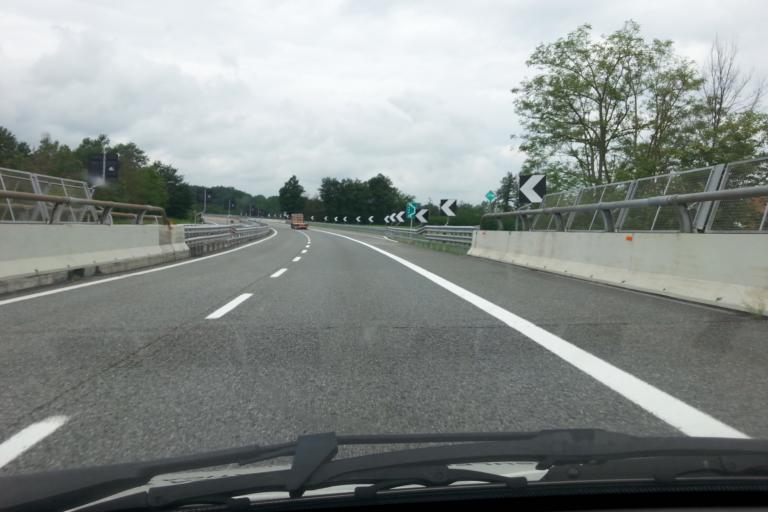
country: IT
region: Piedmont
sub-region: Provincia di Cuneo
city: Lesegno
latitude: 44.4116
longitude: 7.9610
